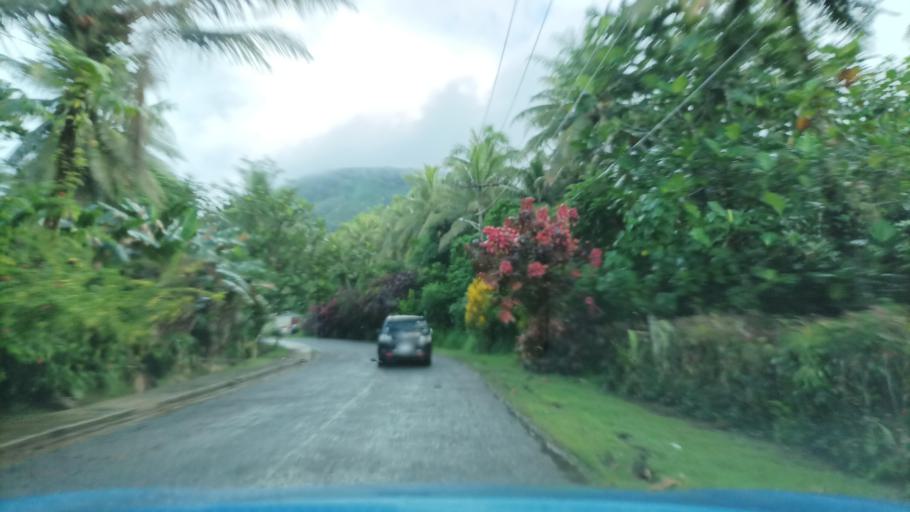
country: FM
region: Pohnpei
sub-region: Sokehs Municipality
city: Palikir - National Government Center
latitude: 6.9244
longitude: 158.1649
